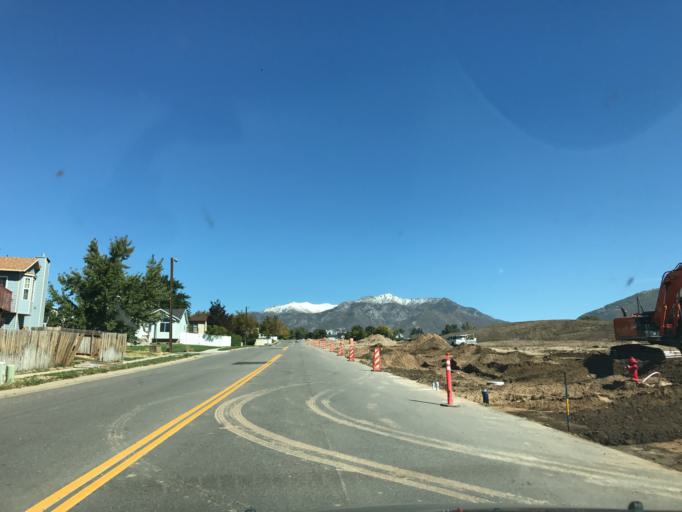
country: US
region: Utah
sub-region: Davis County
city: Hill Air Force Bace
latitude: 41.0929
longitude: -111.9423
